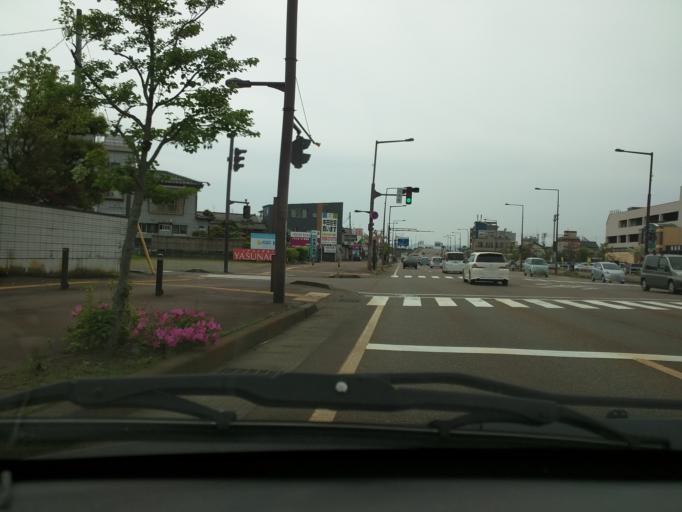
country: JP
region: Niigata
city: Nagaoka
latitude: 37.4499
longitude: 138.8415
